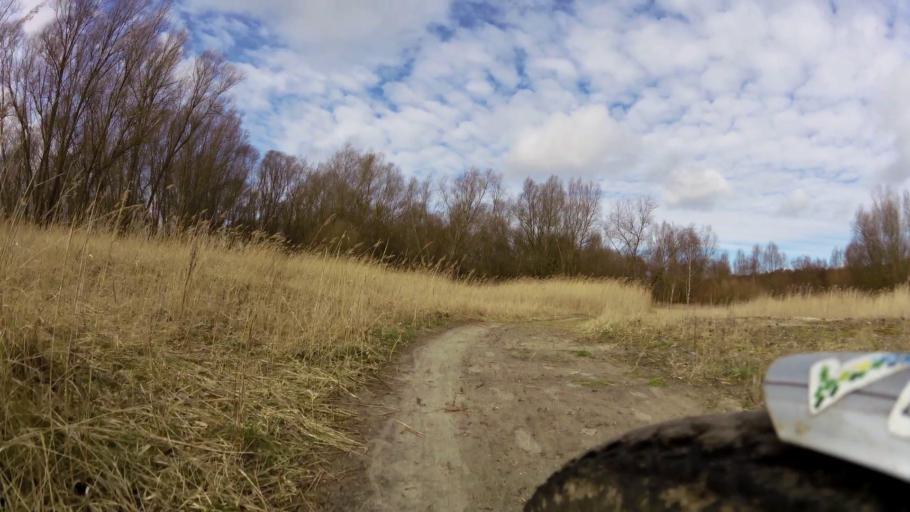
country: PL
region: West Pomeranian Voivodeship
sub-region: Powiat kamienski
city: Kamien Pomorski
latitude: 53.9793
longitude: 14.7698
